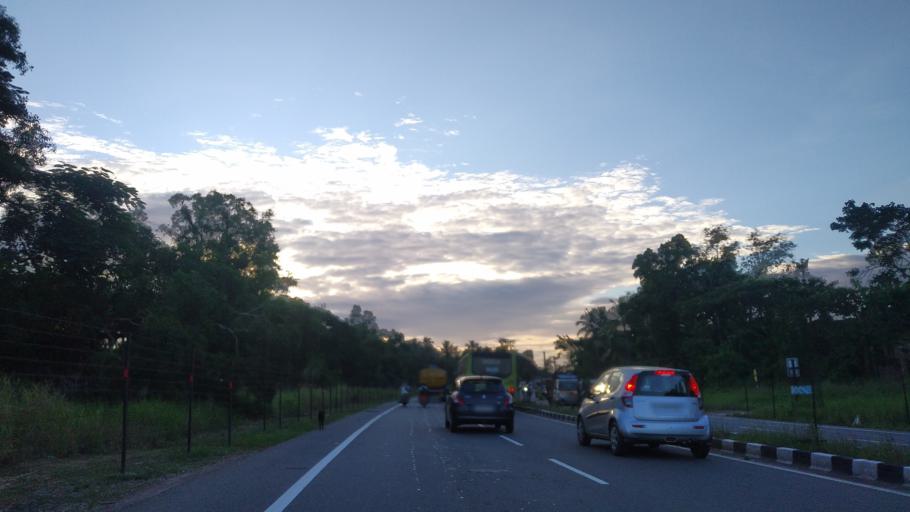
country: IN
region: Kerala
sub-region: Ernakulam
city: Elur
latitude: 10.0684
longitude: 76.3109
